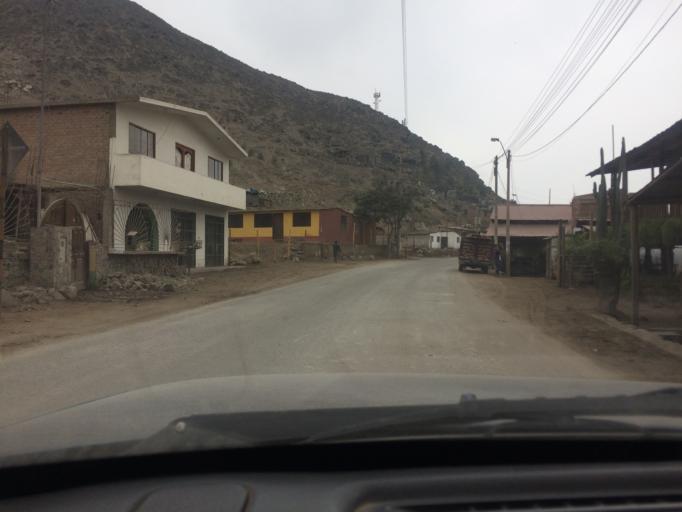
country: PE
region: Lima
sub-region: Lima
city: Cieneguilla
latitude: -12.1848
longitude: -76.8661
